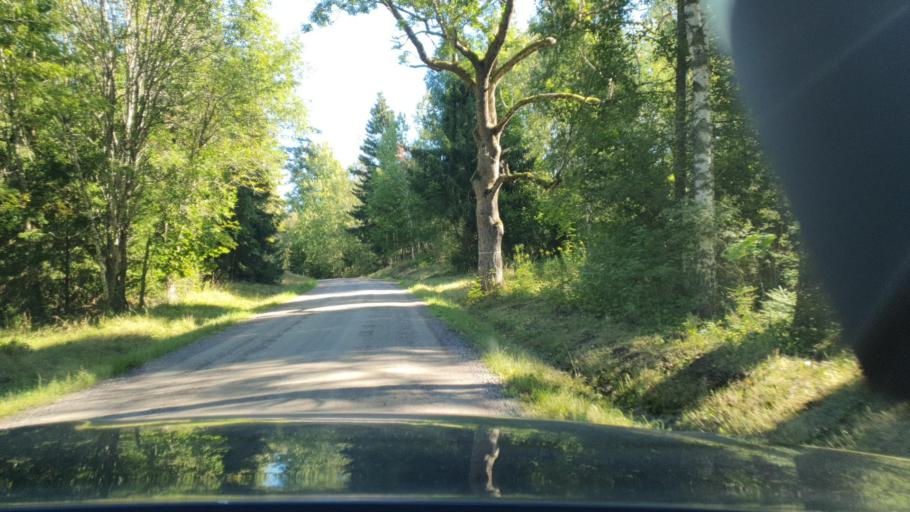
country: SE
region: Vaermland
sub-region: Kristinehamns Kommun
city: Bjorneborg
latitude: 59.2097
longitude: 14.2320
